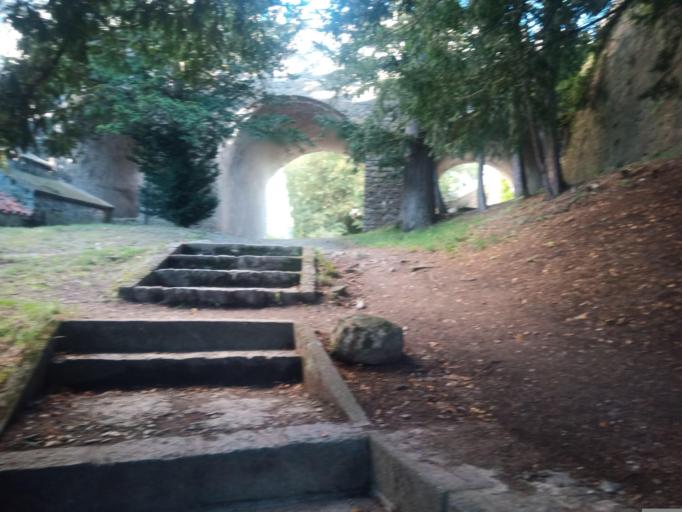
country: CZ
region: Jihocesky
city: Kovarov
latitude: 49.5131
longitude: 14.1698
